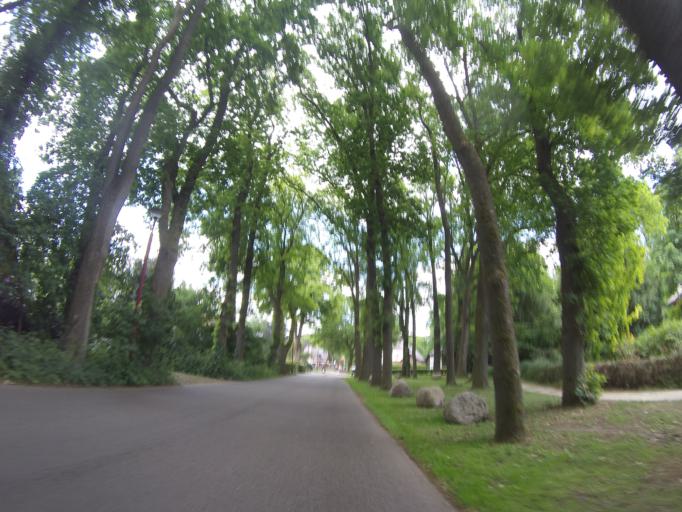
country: NL
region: Gelderland
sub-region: Gemeente Ede
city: Harskamp
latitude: 52.1837
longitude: 5.7692
